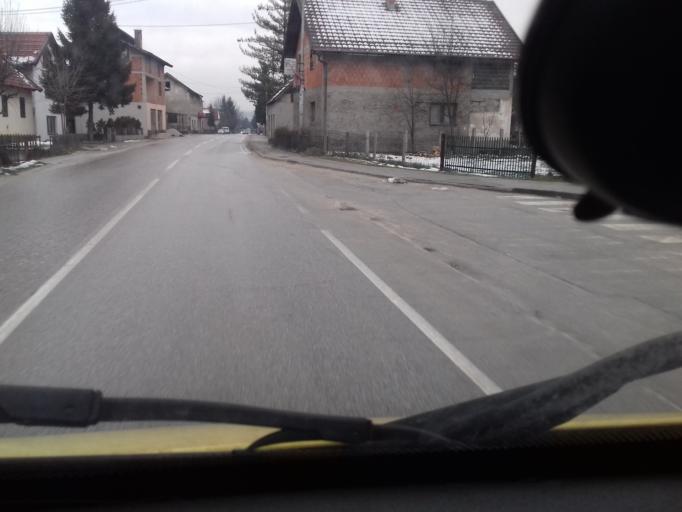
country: BA
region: Federation of Bosnia and Herzegovina
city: Vitez
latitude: 44.1604
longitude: 17.7835
